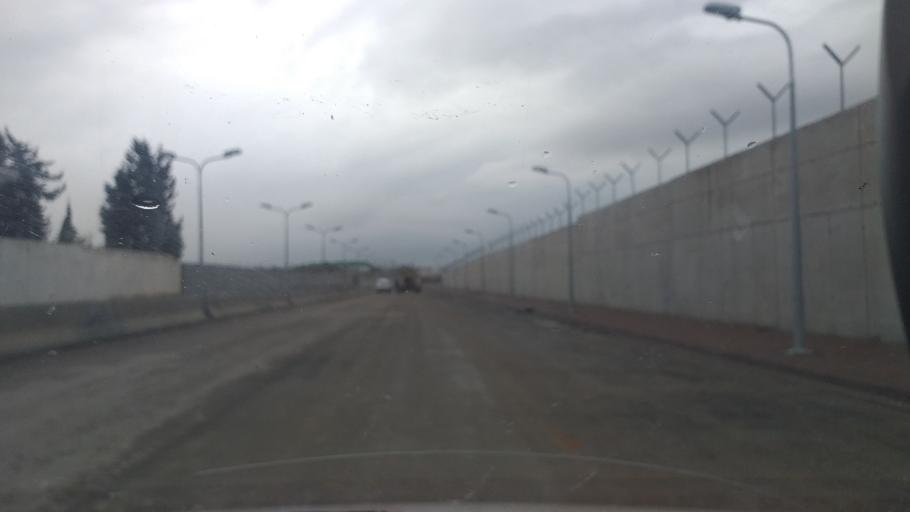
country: TN
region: Ariana
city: Ariana
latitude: 36.8548
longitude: 10.2129
